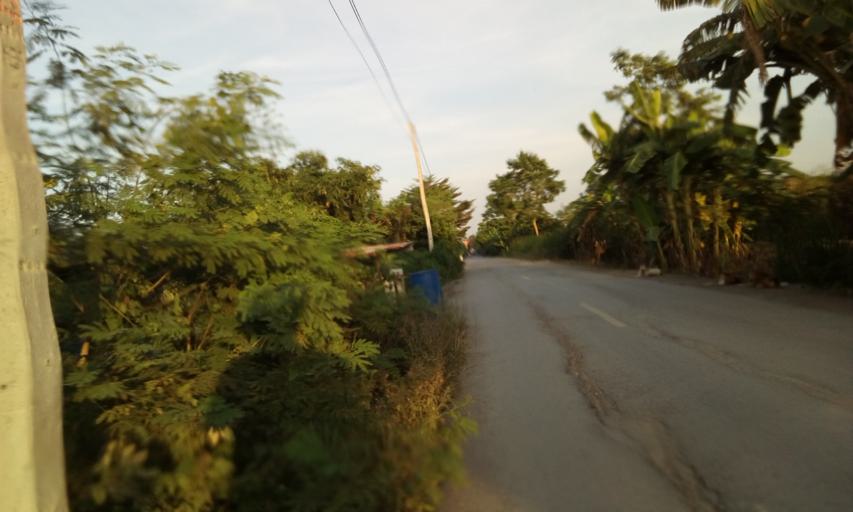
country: TH
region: Pathum Thani
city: Ban Lam Luk Ka
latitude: 14.0368
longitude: 100.8618
